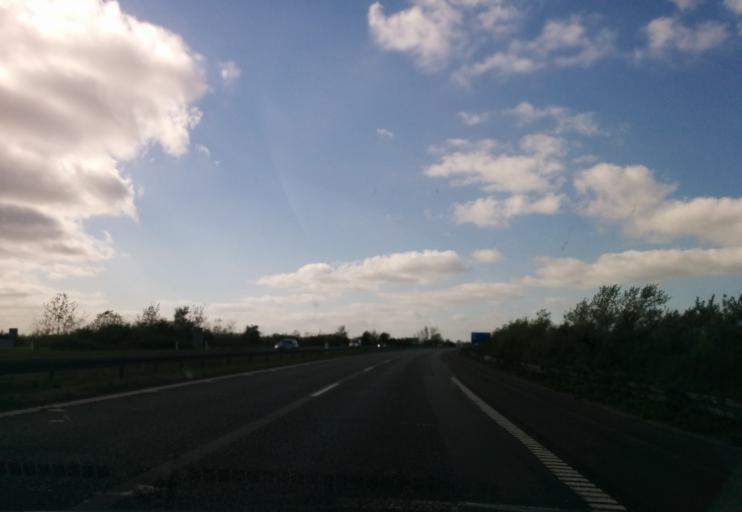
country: DK
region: South Denmark
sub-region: Middelfart Kommune
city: Norre Aby
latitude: 55.4660
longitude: 9.9025
